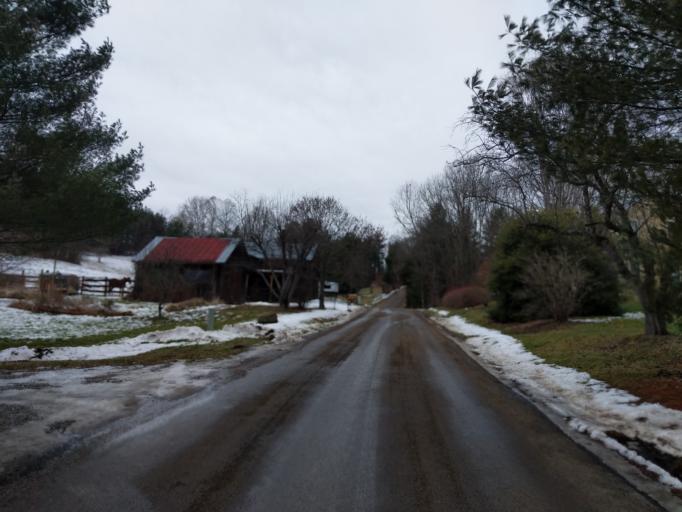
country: US
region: Ohio
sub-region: Athens County
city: The Plains
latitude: 39.3307
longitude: -82.1408
